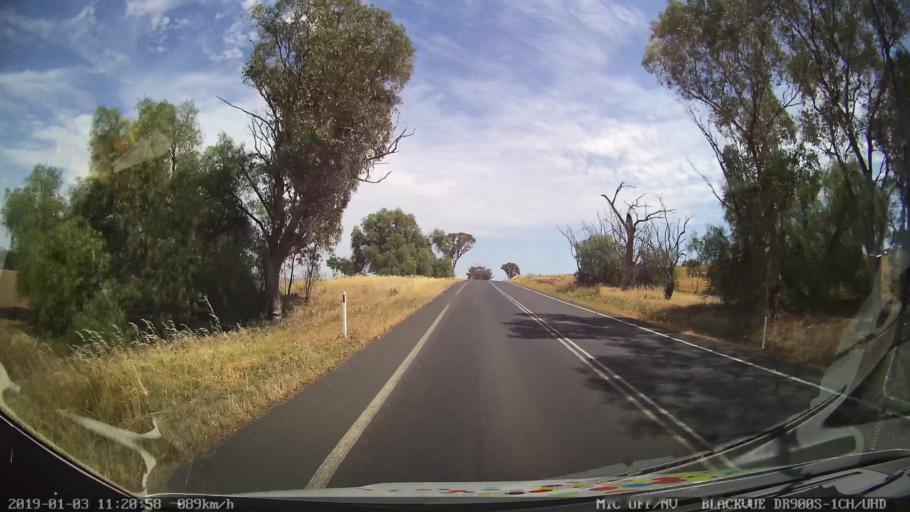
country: AU
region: New South Wales
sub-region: Weddin
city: Grenfell
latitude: -34.0945
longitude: 148.2525
